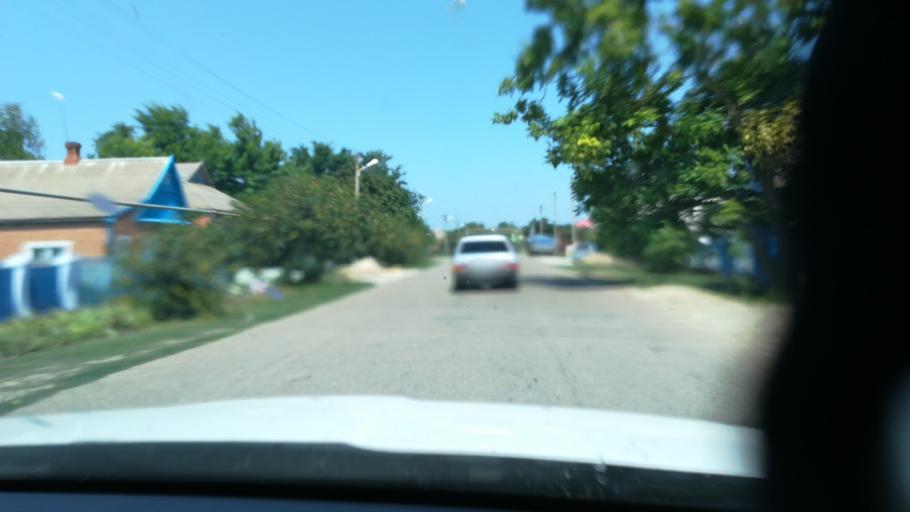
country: RU
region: Krasnodarskiy
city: Starotitarovskaya
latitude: 45.2152
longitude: 37.1429
